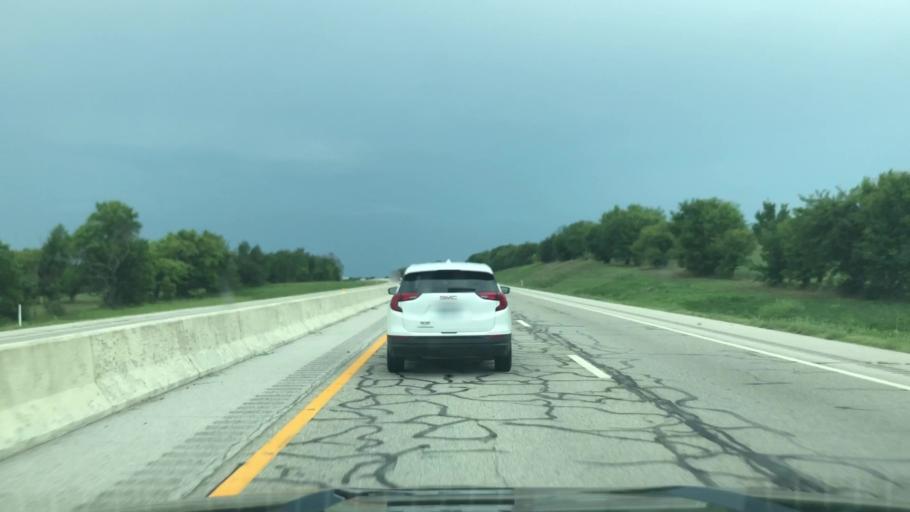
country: US
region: Oklahoma
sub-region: Rogers County
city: Chelsea
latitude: 36.4494
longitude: -95.3682
